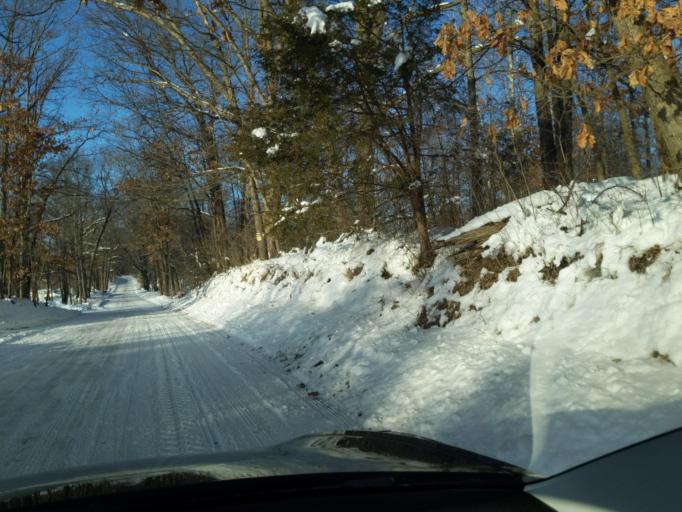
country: US
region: Michigan
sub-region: Ingham County
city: Stockbridge
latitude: 42.4491
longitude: -84.1035
